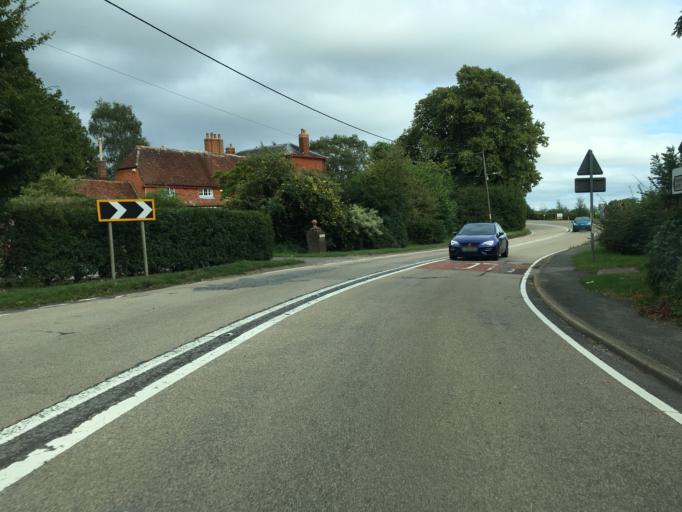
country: GB
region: England
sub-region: Hampshire
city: Petersfield
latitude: 51.0085
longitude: -0.9656
